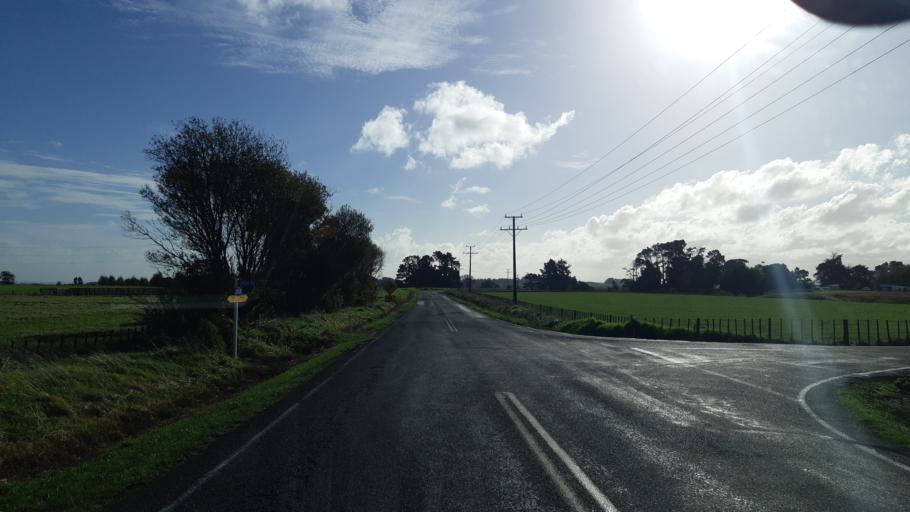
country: NZ
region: Manawatu-Wanganui
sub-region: Wanganui District
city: Wanganui
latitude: -39.9407
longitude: 175.1288
